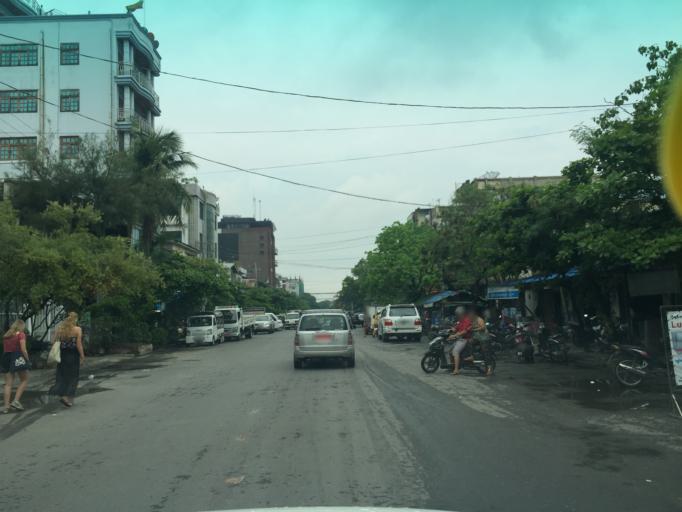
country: MM
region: Mandalay
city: Mandalay
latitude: 21.9772
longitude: 96.0821
